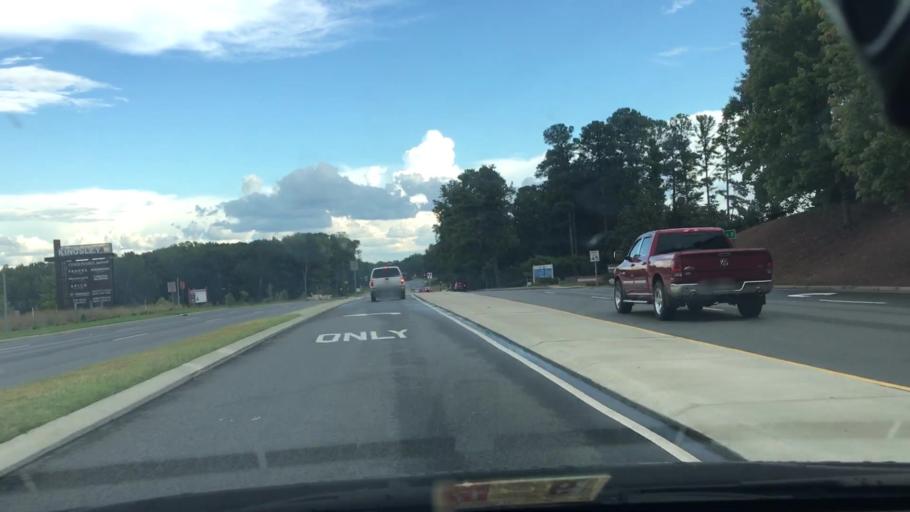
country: US
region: South Carolina
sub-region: York County
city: Fort Mill
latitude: 35.0263
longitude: -80.9638
